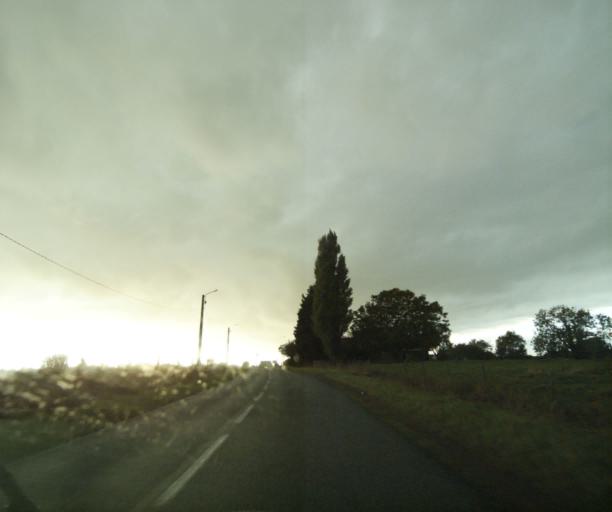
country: FR
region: Nord-Pas-de-Calais
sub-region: Departement du Nord
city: Bousbecque
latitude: 50.7618
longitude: 3.1014
